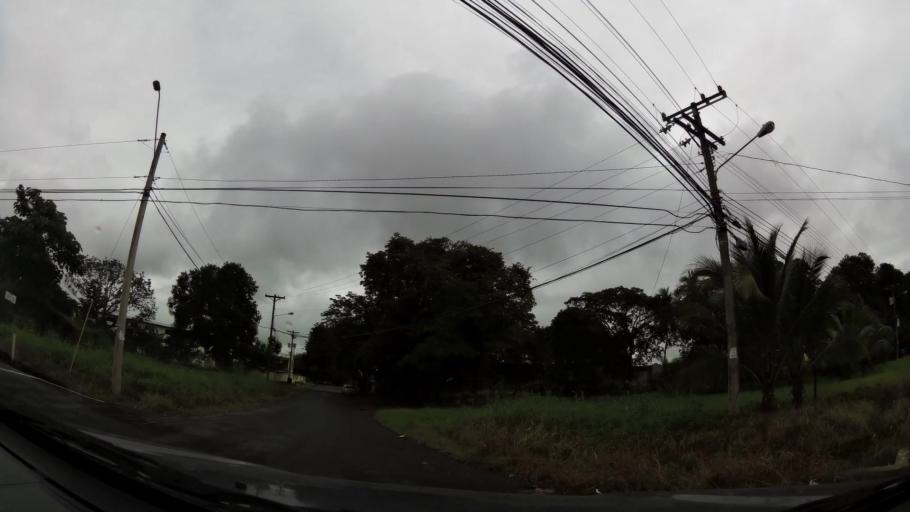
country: PA
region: Chiriqui
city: David
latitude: 8.4343
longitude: -82.4430
